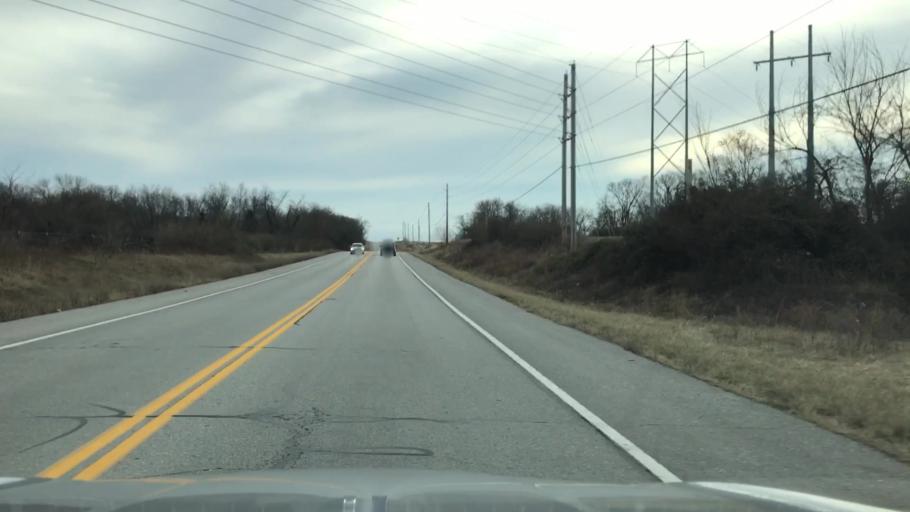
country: US
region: Missouri
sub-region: Jackson County
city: Lees Summit
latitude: 38.8953
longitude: -94.4146
